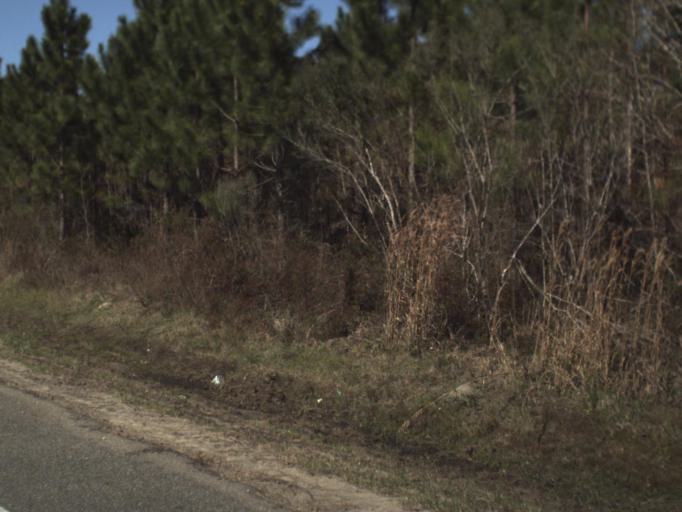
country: US
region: Florida
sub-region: Calhoun County
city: Blountstown
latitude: 30.4610
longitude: -85.0664
